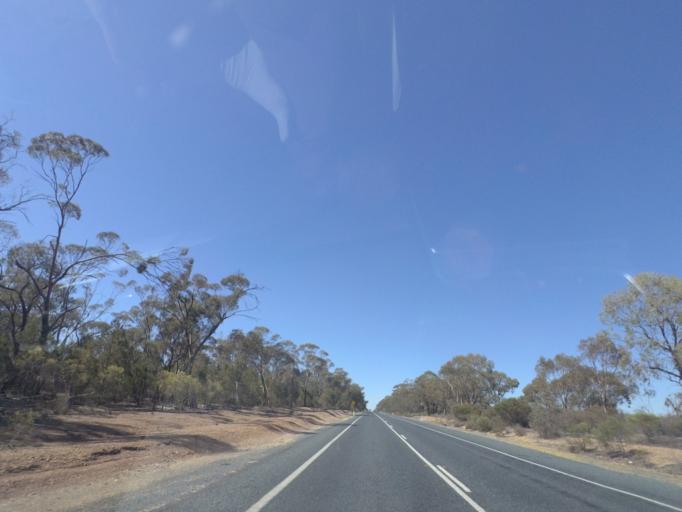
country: AU
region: New South Wales
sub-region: Bland
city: West Wyalong
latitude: -34.1237
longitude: 147.1263
